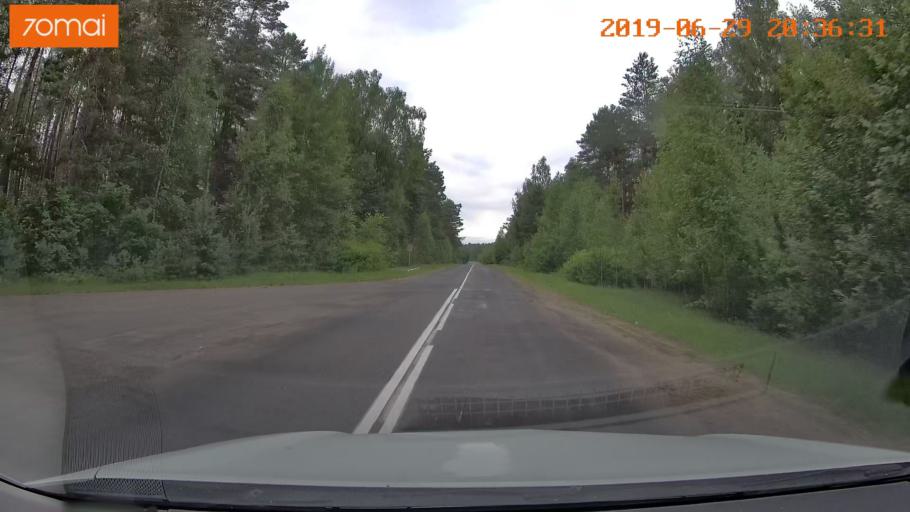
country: BY
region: Brest
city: Hantsavichy
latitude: 52.5272
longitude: 26.3592
